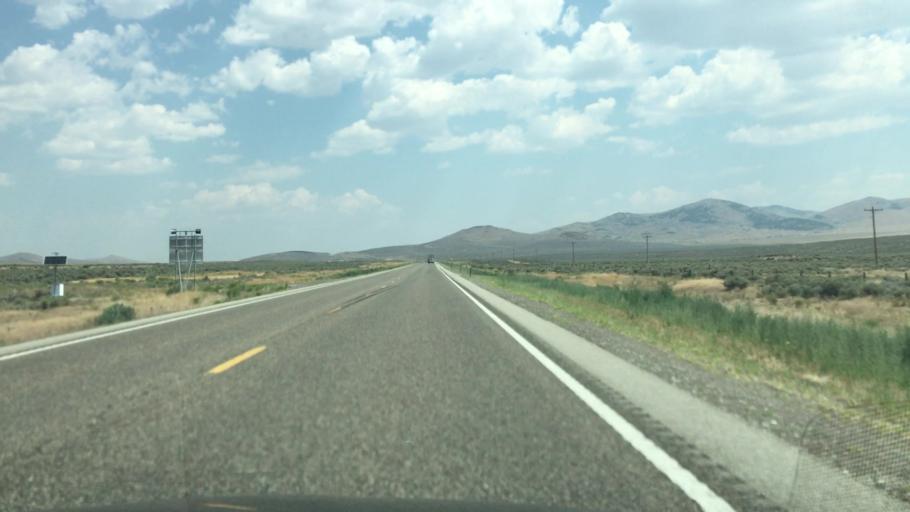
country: US
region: Nevada
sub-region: Elko County
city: Wells
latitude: 41.1538
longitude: -114.9000
